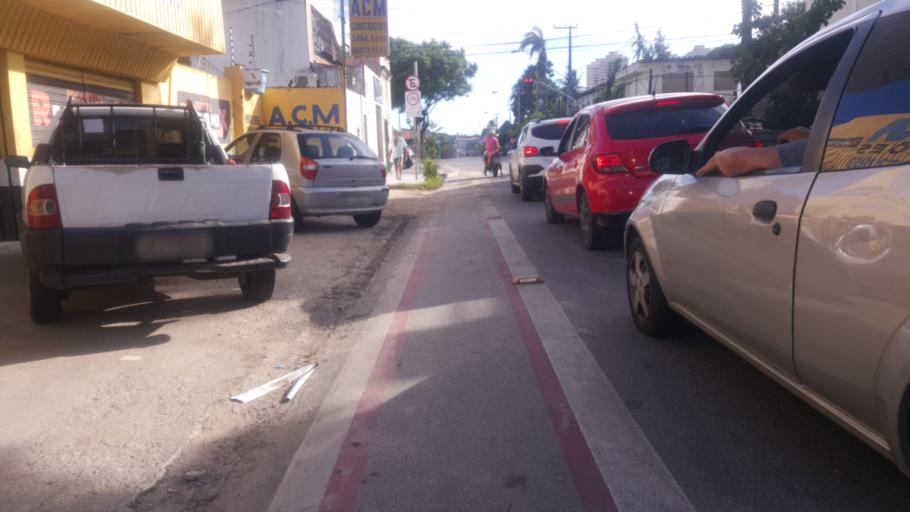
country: BR
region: Ceara
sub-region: Fortaleza
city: Fortaleza
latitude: -3.7532
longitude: -38.5397
